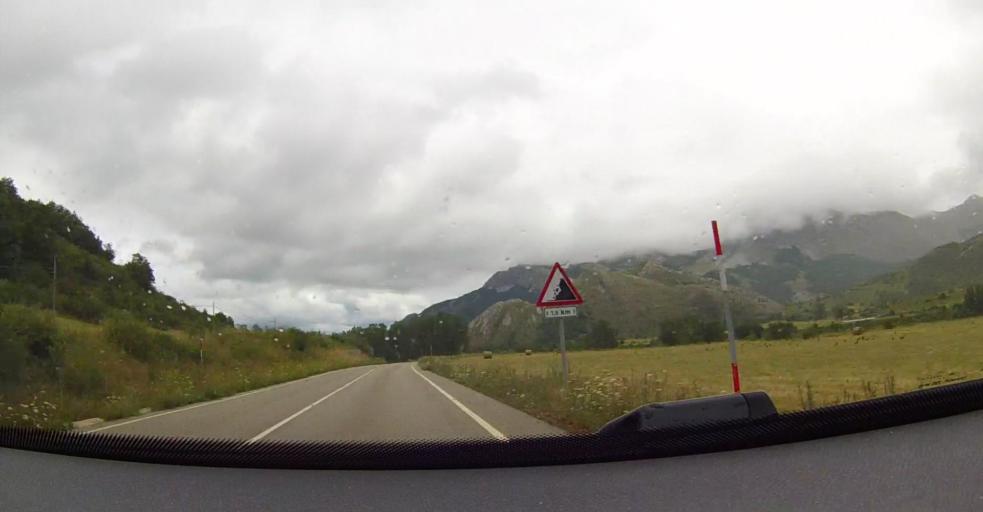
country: ES
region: Castille and Leon
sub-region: Provincia de Leon
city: Buron
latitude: 43.0294
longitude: -5.0728
